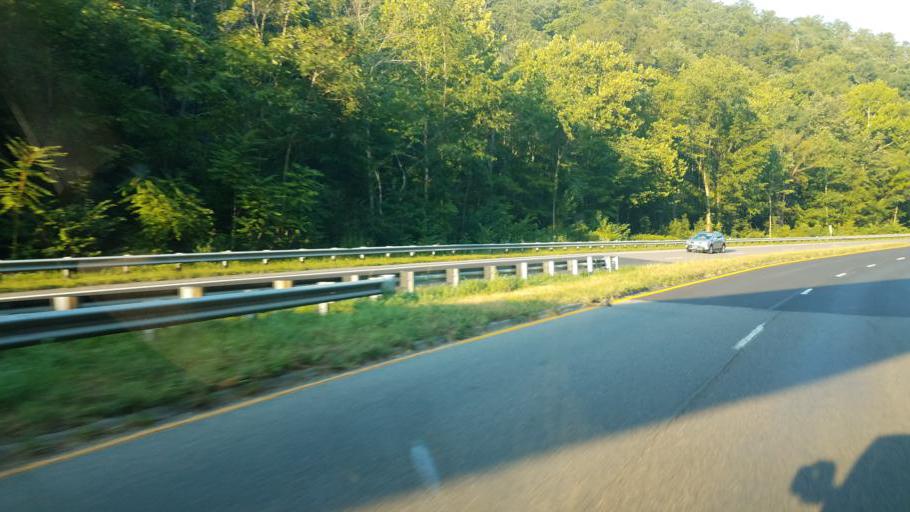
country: US
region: Tennessee
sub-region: Hawkins County
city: Church Hill
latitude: 36.6449
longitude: -82.7461
